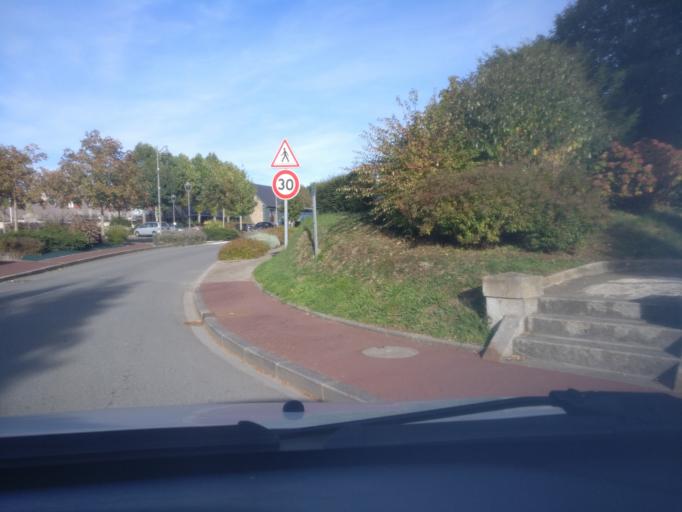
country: FR
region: Lower Normandy
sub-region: Departement de la Manche
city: Marcey-les-Greves
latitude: 48.6970
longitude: -1.3919
